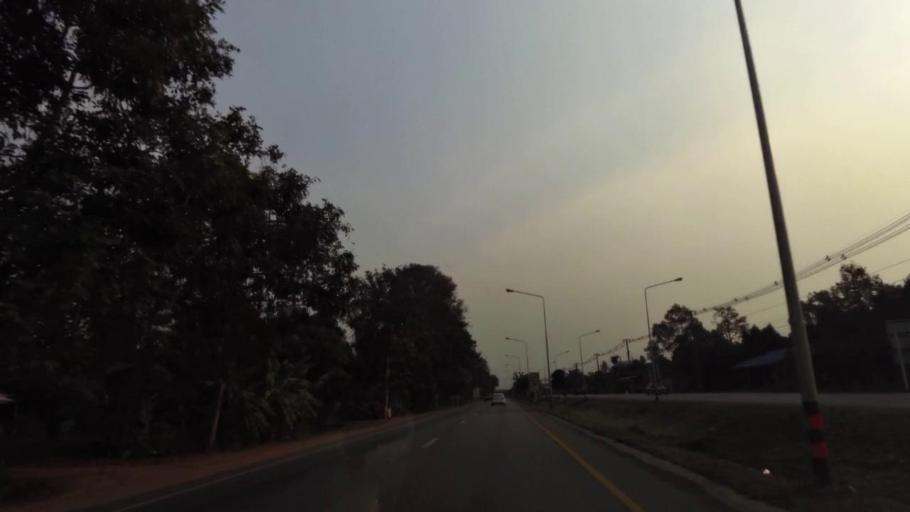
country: TH
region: Chanthaburi
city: Khlung
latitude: 12.5059
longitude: 102.1699
